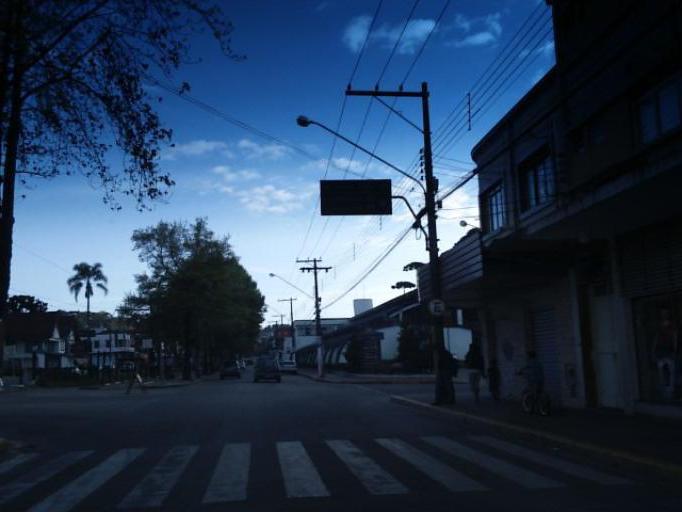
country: BR
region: Sao Paulo
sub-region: Campos Do Jordao
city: Campos do Jordao
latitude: -22.7386
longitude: -45.5925
